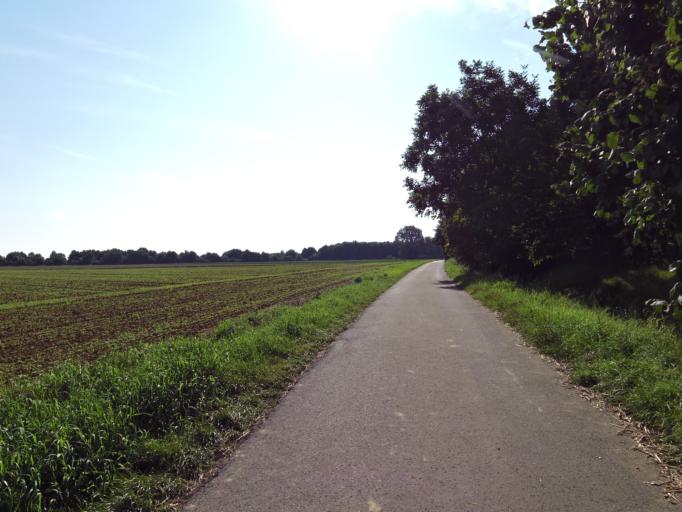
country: DE
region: North Rhine-Westphalia
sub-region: Regierungsbezirk Koln
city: Eschweiler
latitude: 50.8408
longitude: 6.2398
